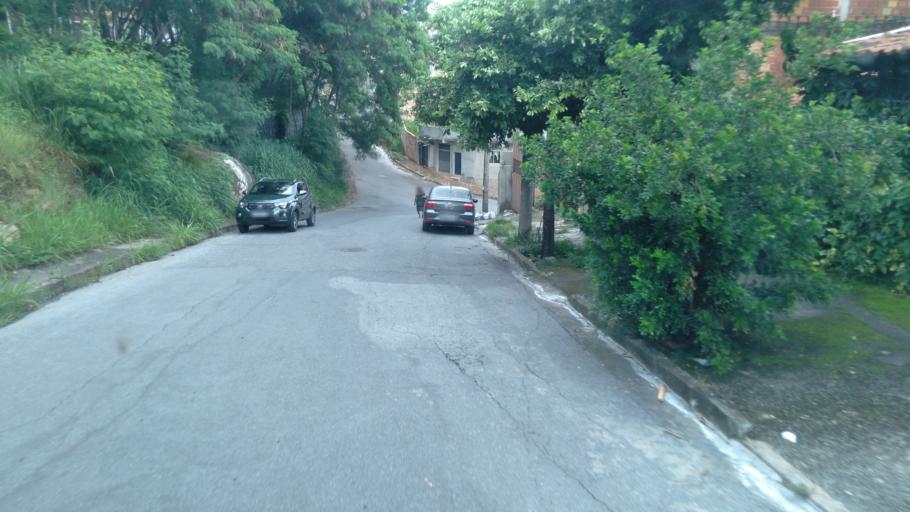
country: BR
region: Minas Gerais
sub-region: Belo Horizonte
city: Belo Horizonte
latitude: -19.8487
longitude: -43.9099
